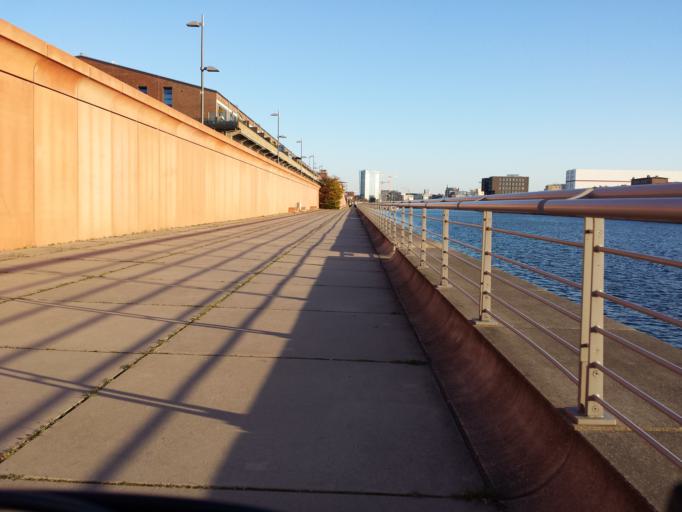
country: DE
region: Bremen
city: Bremen
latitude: 53.0917
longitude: 8.7707
